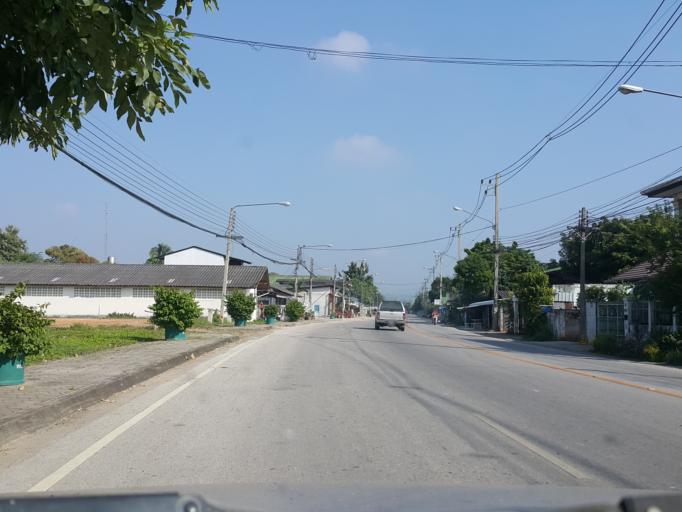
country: TH
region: Chiang Mai
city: San Sai
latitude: 18.8351
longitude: 99.1287
